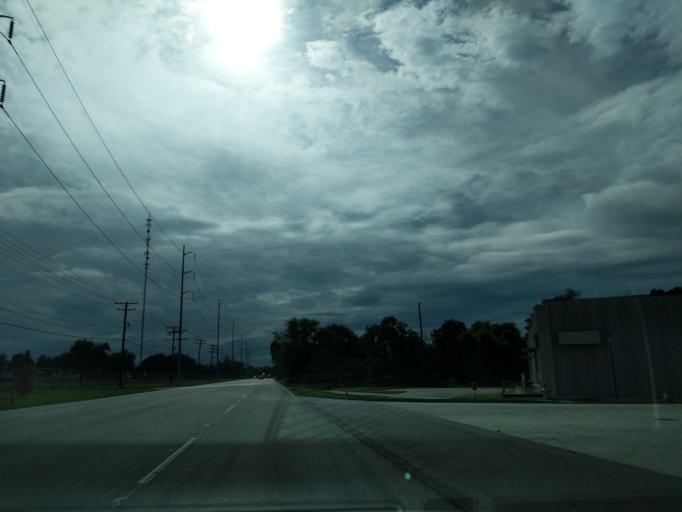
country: US
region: Louisiana
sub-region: Saint Bernard Parish
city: Chalmette
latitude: 30.0225
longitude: -89.9235
